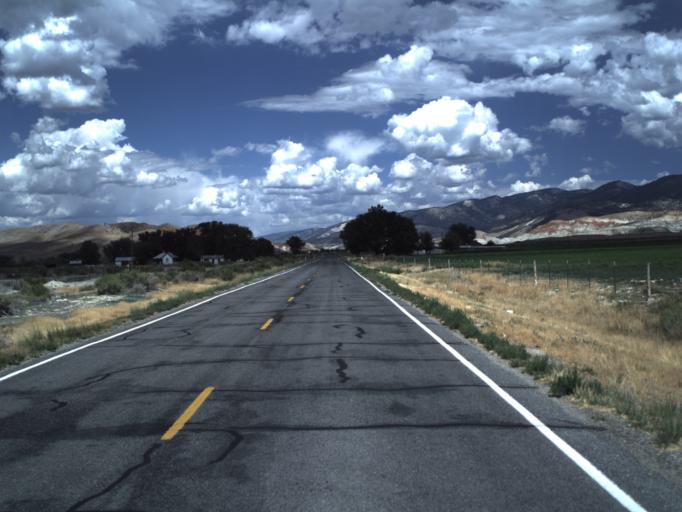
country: US
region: Utah
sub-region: Sanpete County
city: Gunnison
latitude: 39.1403
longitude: -111.7688
